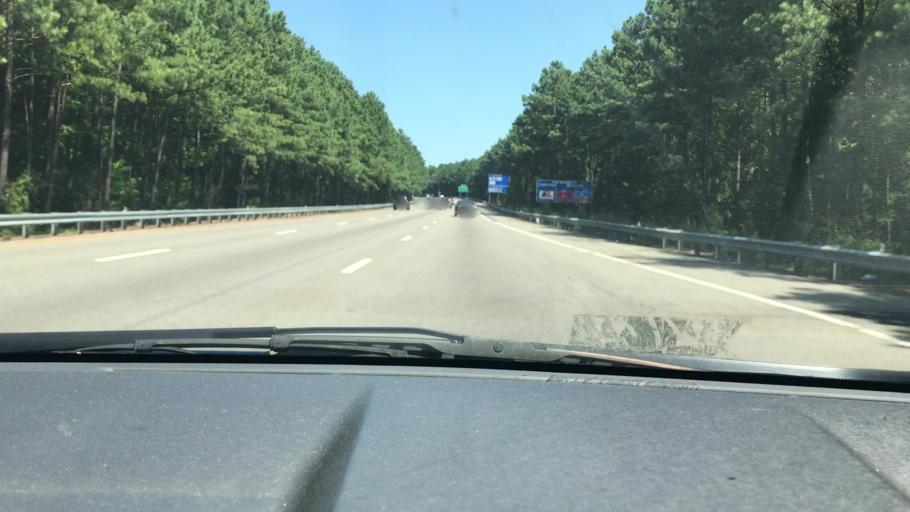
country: US
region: Virginia
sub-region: Henrico County
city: Glen Allen
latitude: 37.6631
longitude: -77.4783
